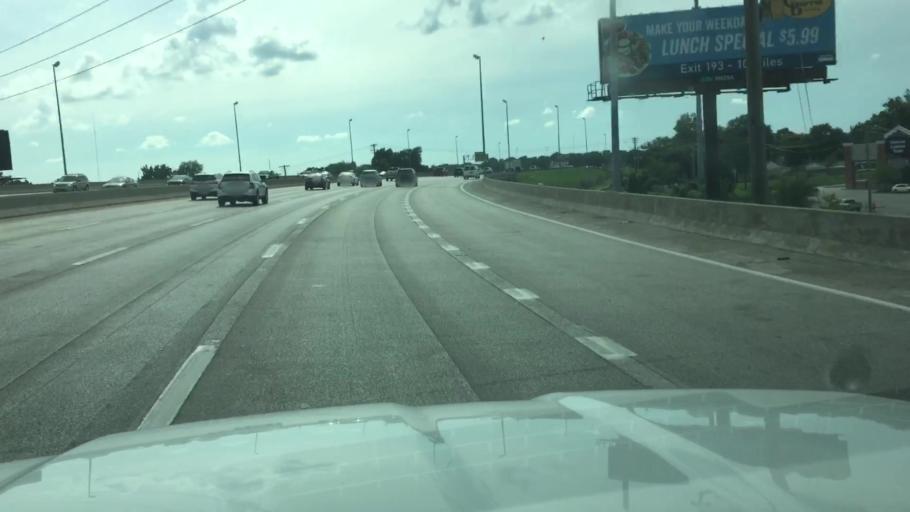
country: US
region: Missouri
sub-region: Saint Louis County
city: Lemay
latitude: 38.5543
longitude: -90.2625
